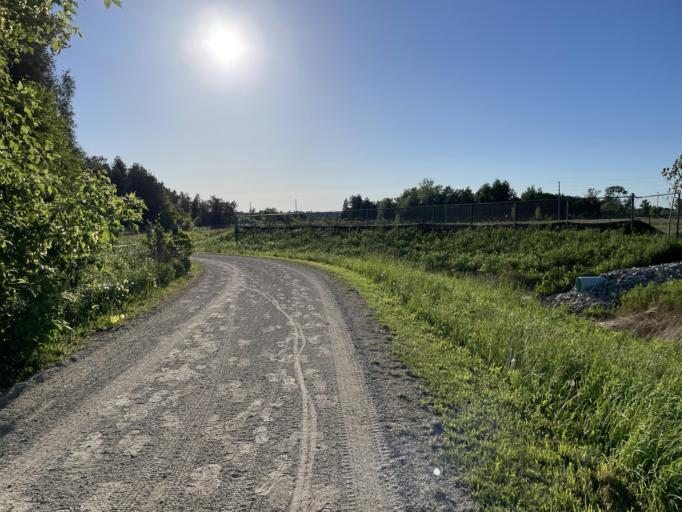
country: CA
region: Ontario
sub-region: Wellington County
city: Guelph
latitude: 43.4928
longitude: -80.2241
